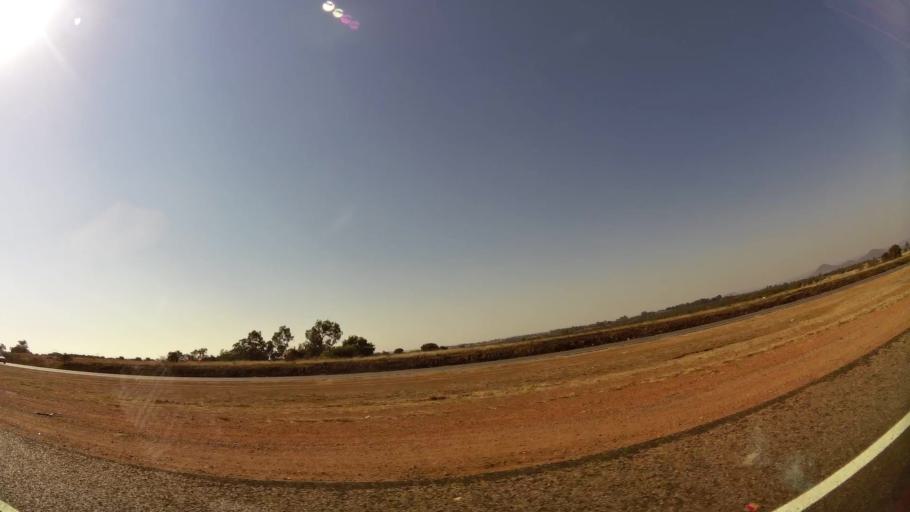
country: ZA
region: Gauteng
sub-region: City of Tshwane Metropolitan Municipality
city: Mabopane
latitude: -25.5708
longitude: 28.1078
